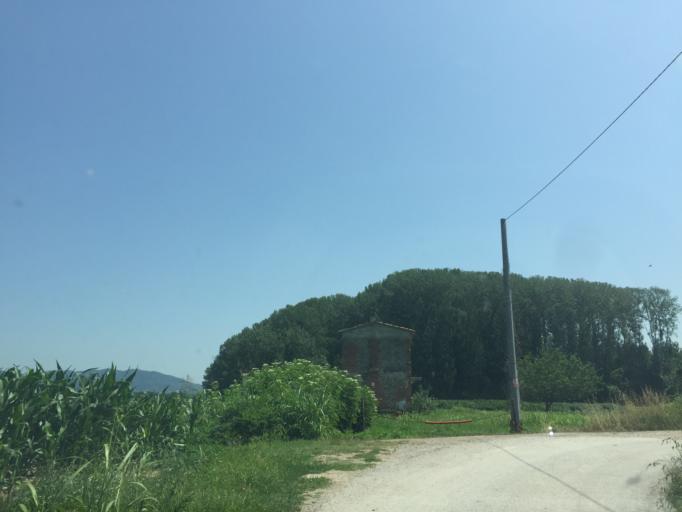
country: IT
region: Tuscany
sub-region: Provincia di Pistoia
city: Anchione
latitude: 43.8206
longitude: 10.7797
